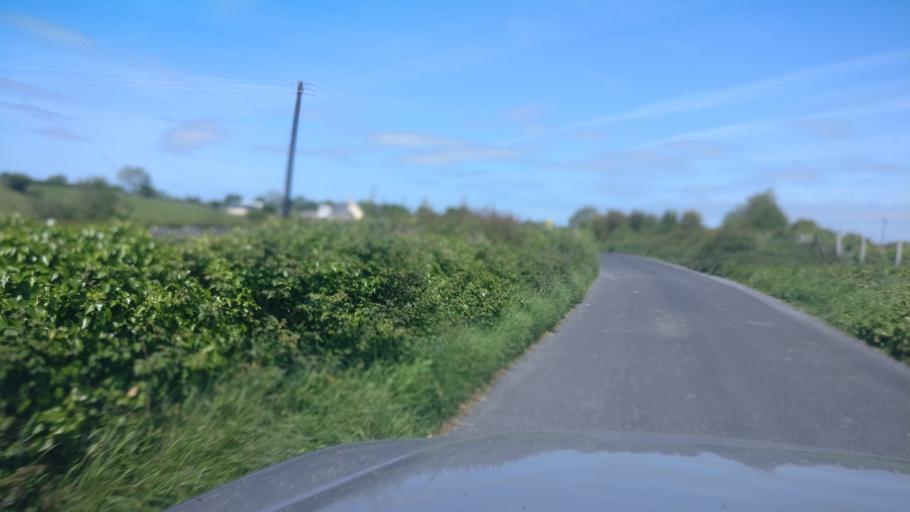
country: IE
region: Connaught
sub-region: County Galway
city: Gort
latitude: 53.0922
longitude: -8.8068
